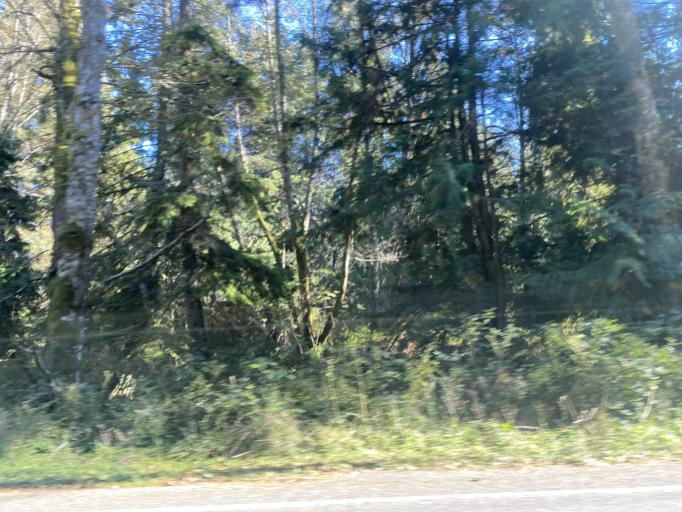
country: US
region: Washington
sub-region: Island County
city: Langley
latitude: 48.0362
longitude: -122.4206
